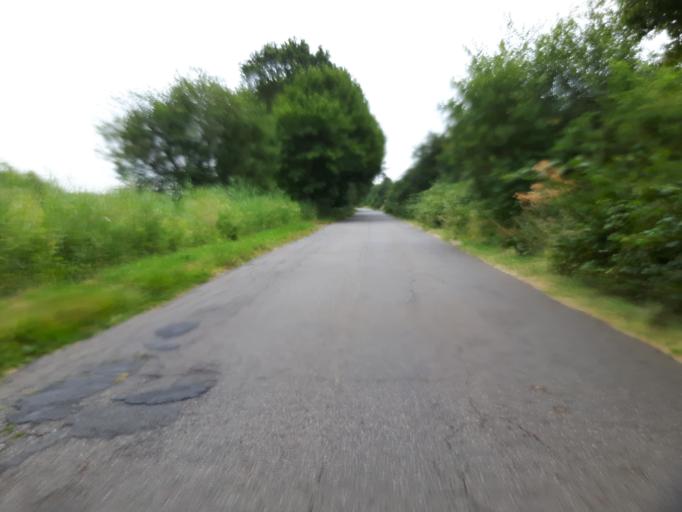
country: DE
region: Lower Saxony
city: Stelle
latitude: 53.3971
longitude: 10.0798
